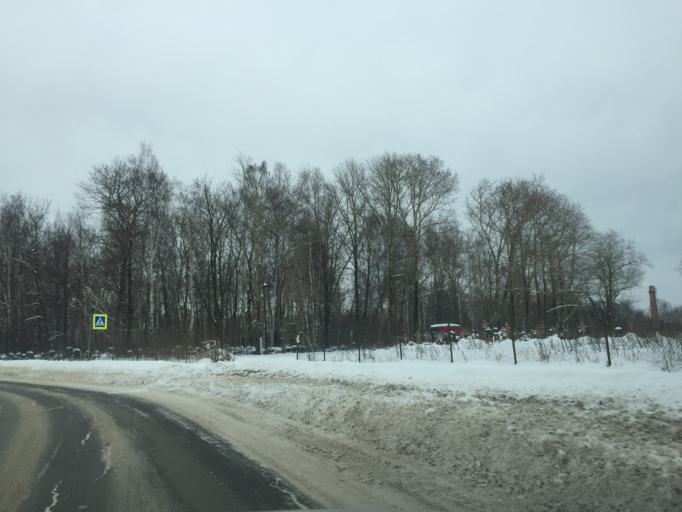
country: RU
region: Leningrad
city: Imeni Sverdlova
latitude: 59.7903
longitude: 30.6858
